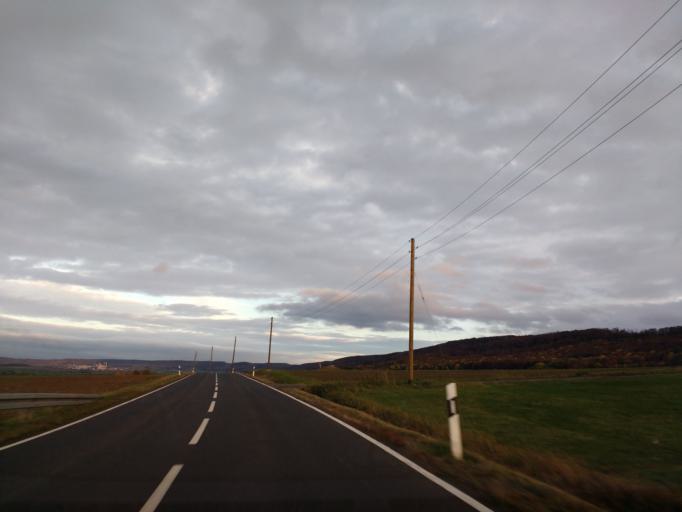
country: DE
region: Thuringia
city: Kleinbartloff
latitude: 51.3529
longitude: 10.3753
